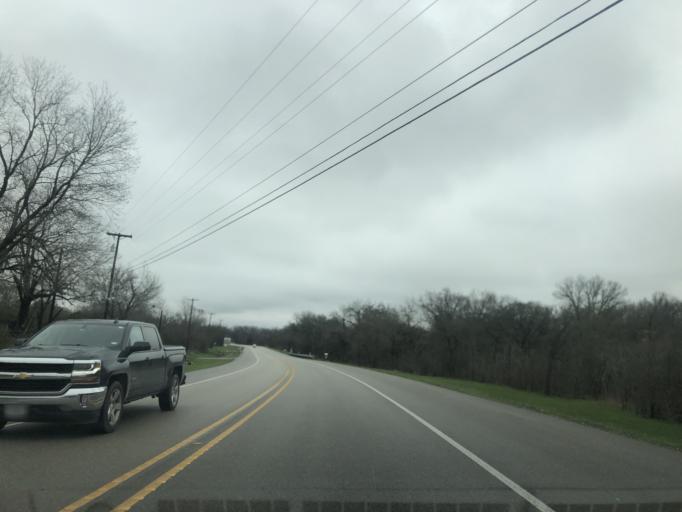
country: US
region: Texas
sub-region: Williamson County
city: Georgetown
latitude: 30.6435
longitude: -97.5775
